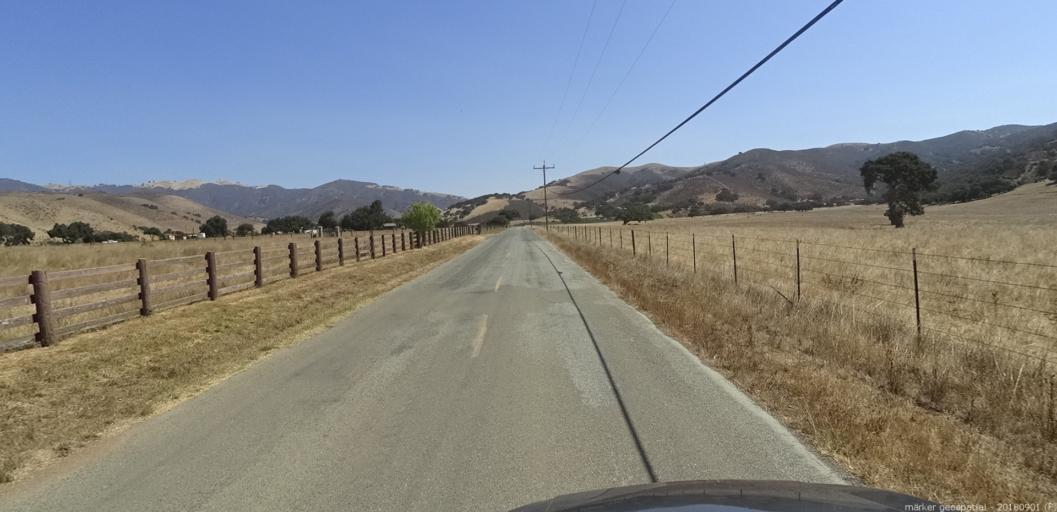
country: US
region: California
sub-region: Monterey County
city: Chualar
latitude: 36.5932
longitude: -121.4439
